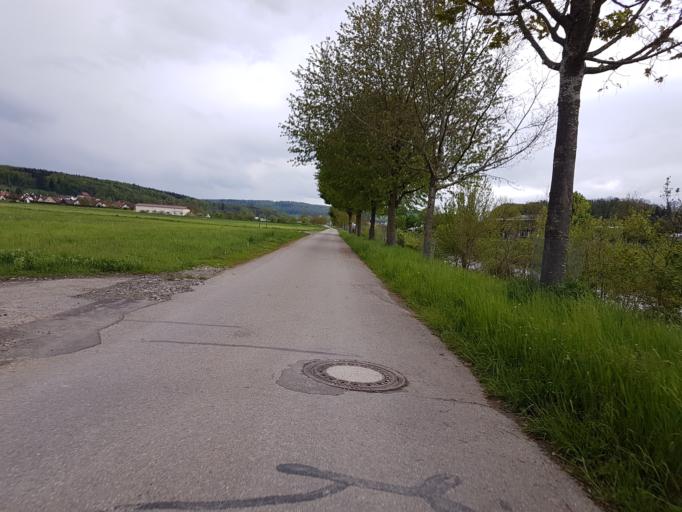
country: DE
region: Baden-Wuerttemberg
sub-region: Freiburg Region
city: Wutoschingen
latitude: 47.6492
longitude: 8.3552
